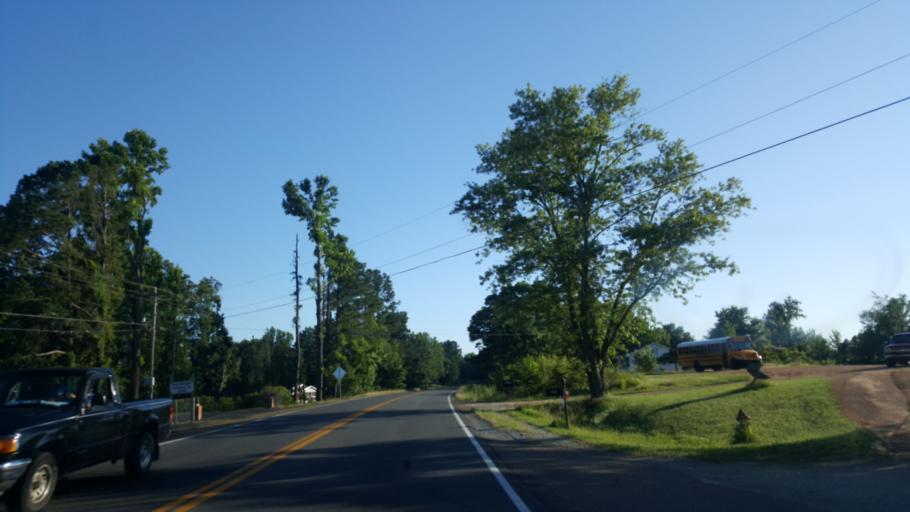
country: US
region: Tennessee
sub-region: Henderson County
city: Lexington
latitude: 35.5894
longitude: -88.3900
